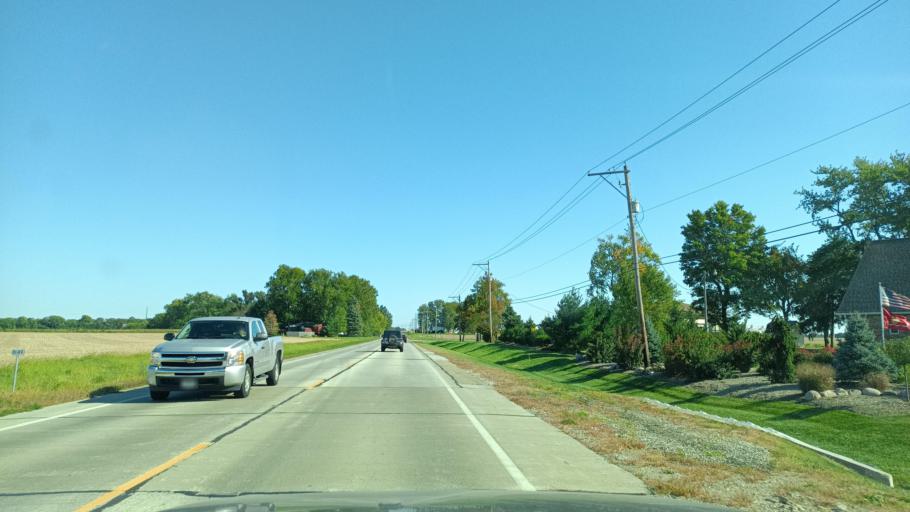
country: US
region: Illinois
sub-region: Champaign County
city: Lake of the Woods
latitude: 40.1686
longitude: -88.3323
